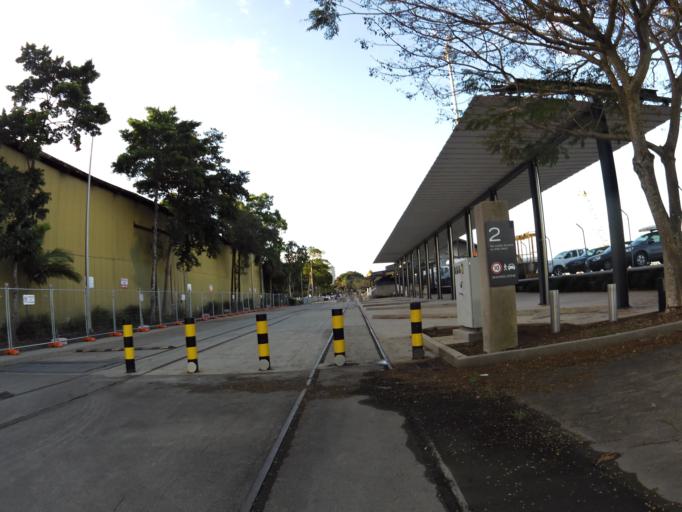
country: AU
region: Queensland
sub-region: Cairns
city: Cairns
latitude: -16.9278
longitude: 145.7798
